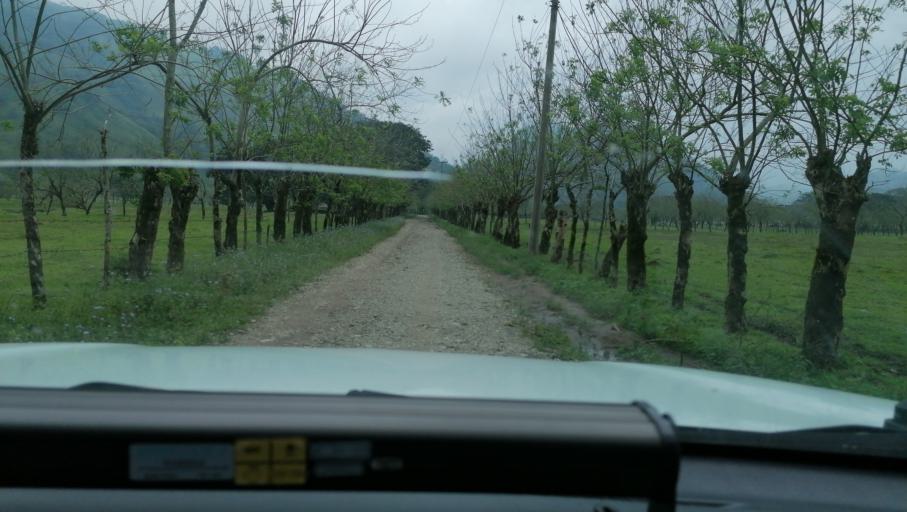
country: MX
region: Chiapas
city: Ixtacomitan
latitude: 17.3657
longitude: -93.1782
